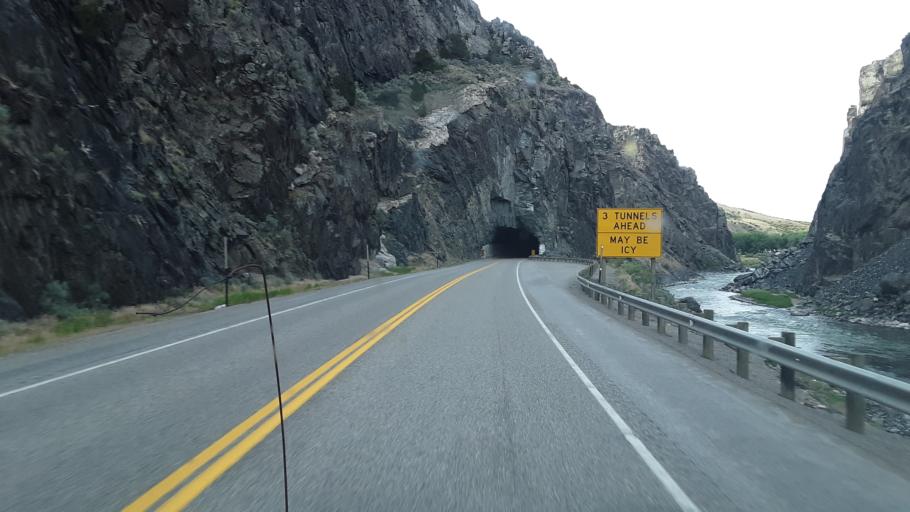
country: US
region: Wyoming
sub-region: Hot Springs County
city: Thermopolis
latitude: 43.4486
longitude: -108.1689
